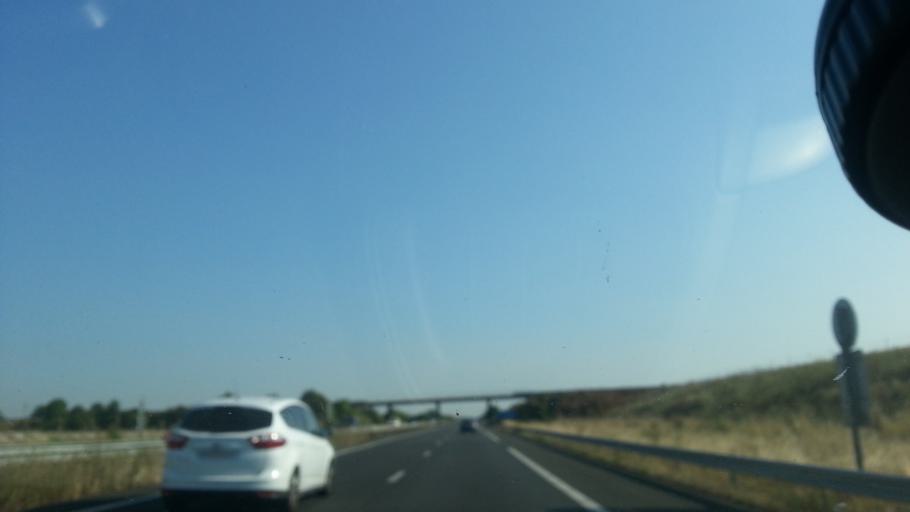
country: FR
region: Centre
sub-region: Departement d'Indre-et-Loire
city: La Celle-Saint-Avant
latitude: 47.0094
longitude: 0.5577
